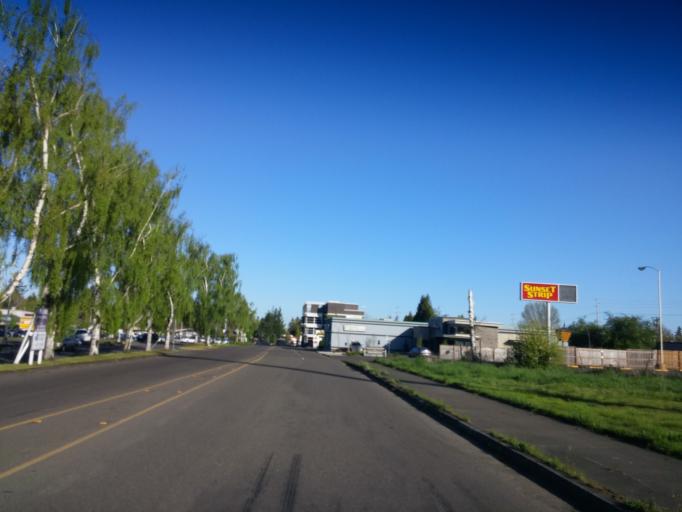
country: US
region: Oregon
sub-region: Washington County
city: West Haven
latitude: 45.5077
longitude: -122.7809
